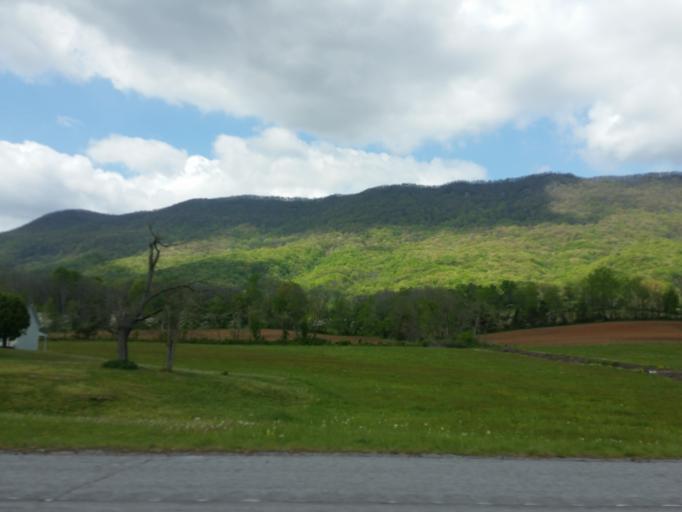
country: US
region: Tennessee
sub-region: Campbell County
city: Fincastle
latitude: 36.4487
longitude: -83.9302
